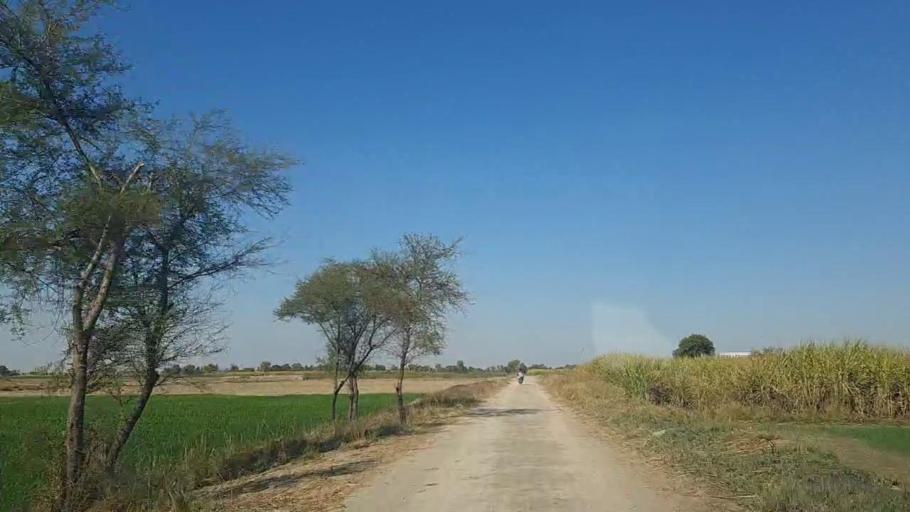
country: PK
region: Sindh
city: Sanghar
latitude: 26.2242
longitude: 68.9648
